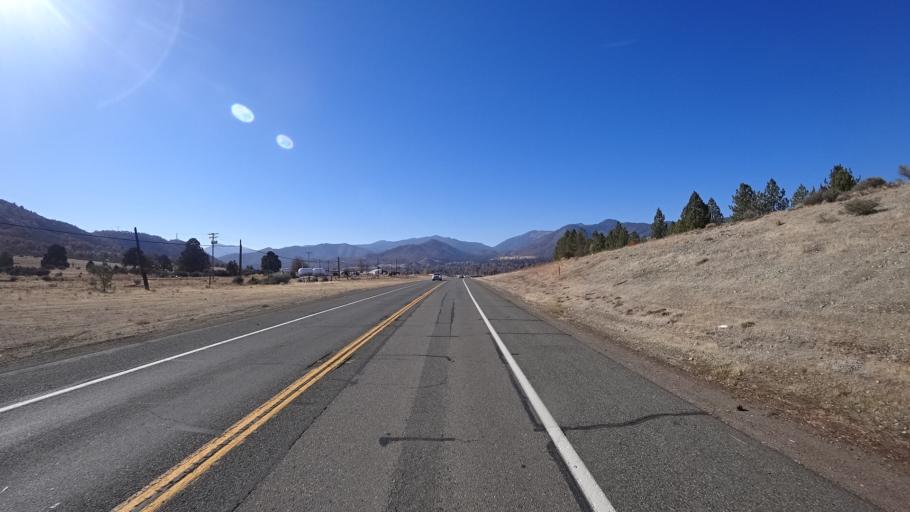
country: US
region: California
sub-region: Siskiyou County
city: Yreka
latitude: 41.7390
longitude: -122.6174
